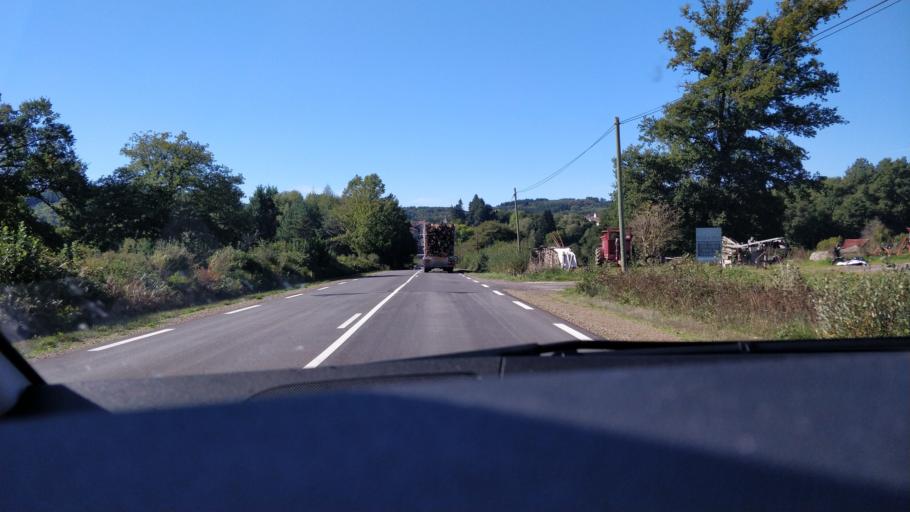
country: FR
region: Limousin
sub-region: Departement de la Haute-Vienne
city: Sauviat-sur-Vige
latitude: 45.9120
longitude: 1.6192
